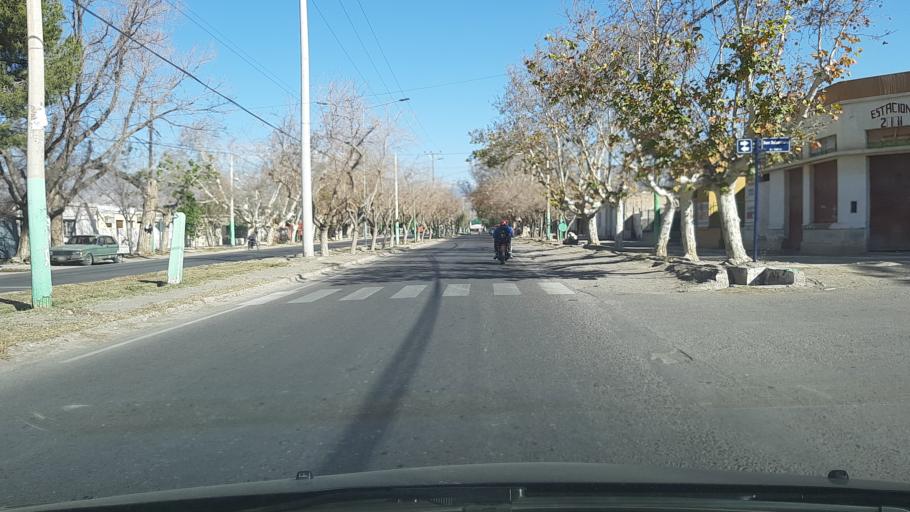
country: AR
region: San Juan
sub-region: Departamento de Rivadavia
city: Rivadavia
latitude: -31.5264
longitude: -68.6323
